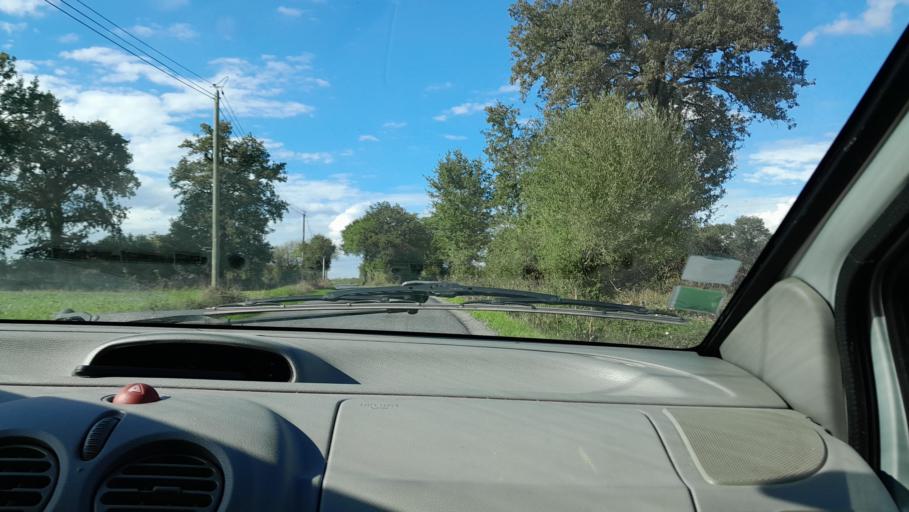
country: FR
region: Pays de la Loire
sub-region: Departement de la Mayenne
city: Ahuille
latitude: 48.0242
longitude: -0.8854
